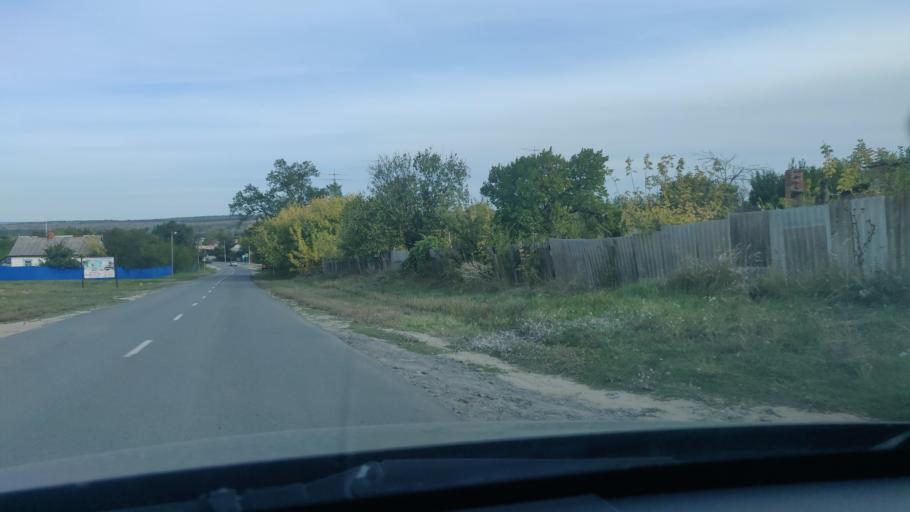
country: RU
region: Rostov
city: Ust'-Donetskiy
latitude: 47.6568
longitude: 40.9056
